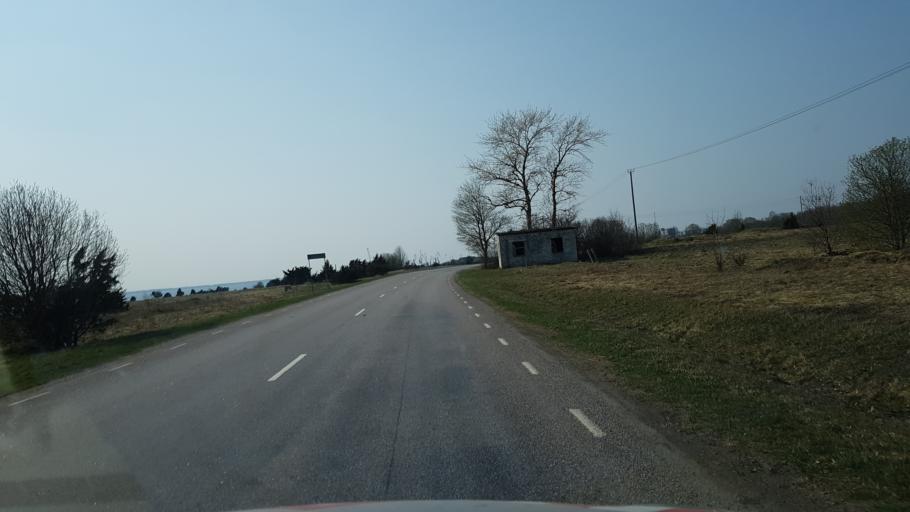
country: EE
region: Harju
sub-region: Paldiski linn
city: Paldiski
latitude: 59.3287
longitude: 24.1108
